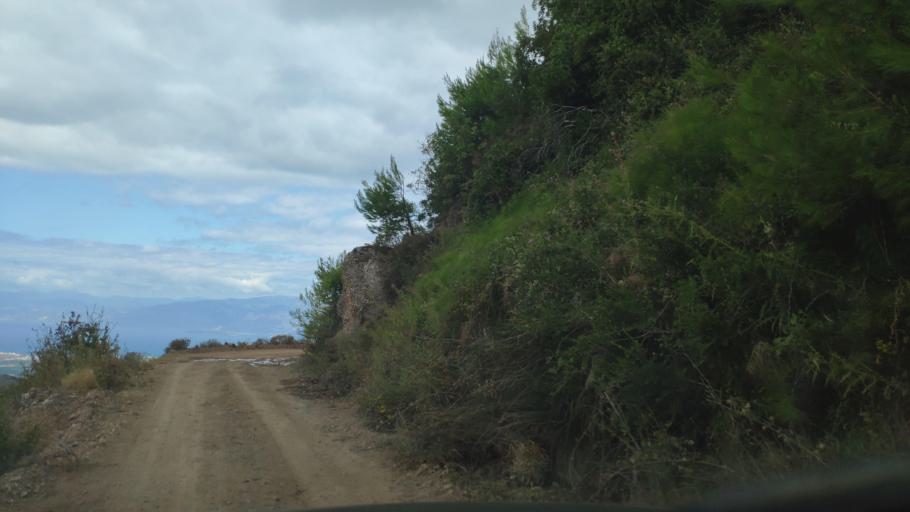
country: GR
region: West Greece
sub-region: Nomos Achaias
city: Temeni
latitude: 38.1691
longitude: 22.1533
